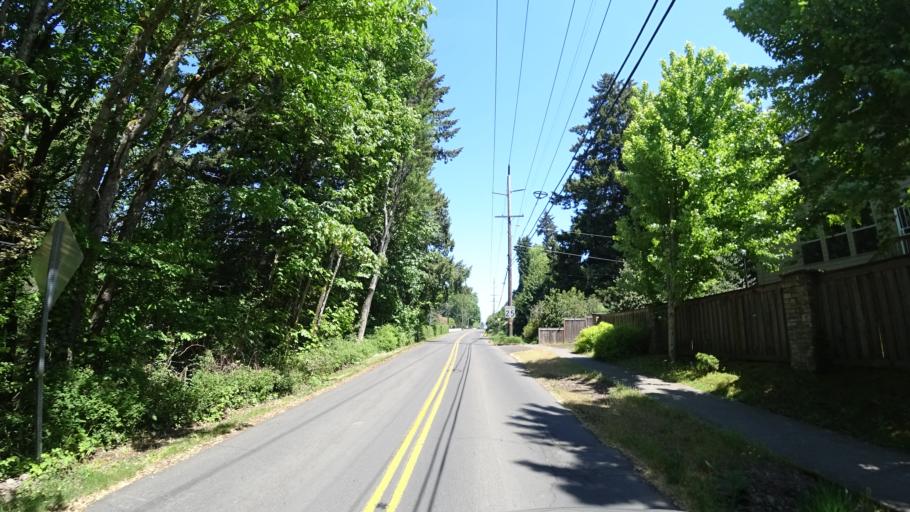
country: US
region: Oregon
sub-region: Washington County
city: Rockcreek
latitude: 45.5230
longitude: -122.9086
